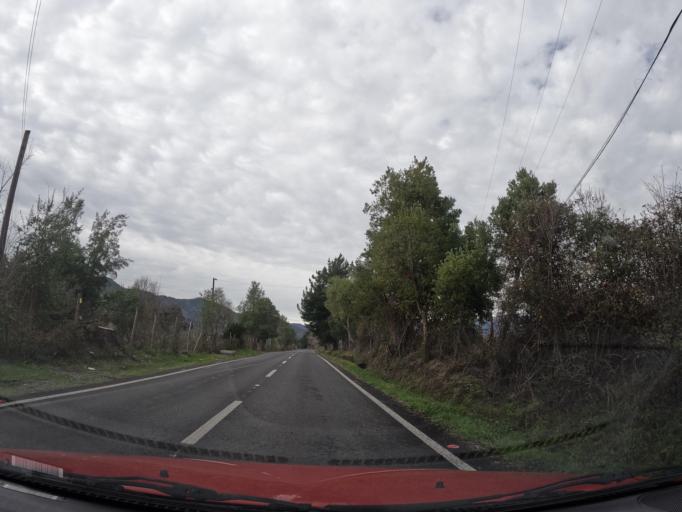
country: CL
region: Maule
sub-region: Provincia de Linares
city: Linares
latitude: -35.9276
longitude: -71.4241
